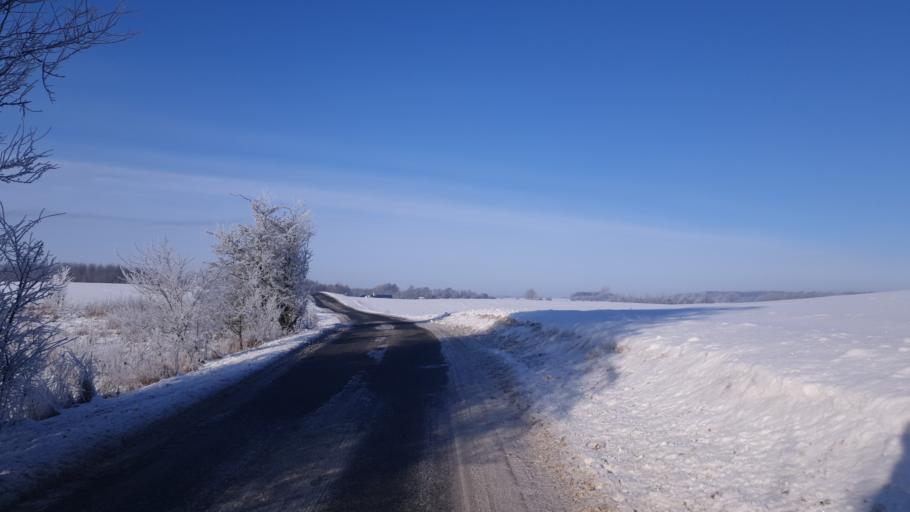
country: DK
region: Central Jutland
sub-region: Hedensted Kommune
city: Hedensted
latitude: 55.8042
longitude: 9.7412
